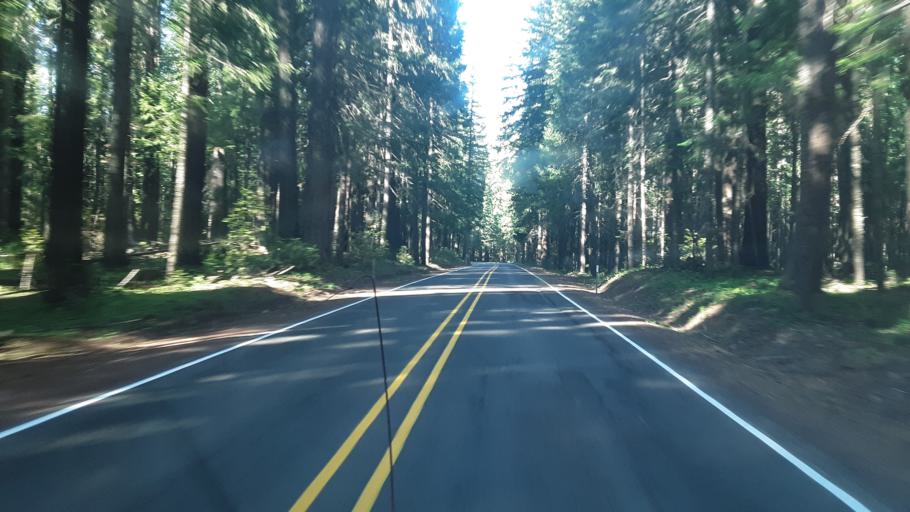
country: US
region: Oregon
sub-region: Jackson County
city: Shady Cove
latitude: 42.9435
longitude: -122.4161
